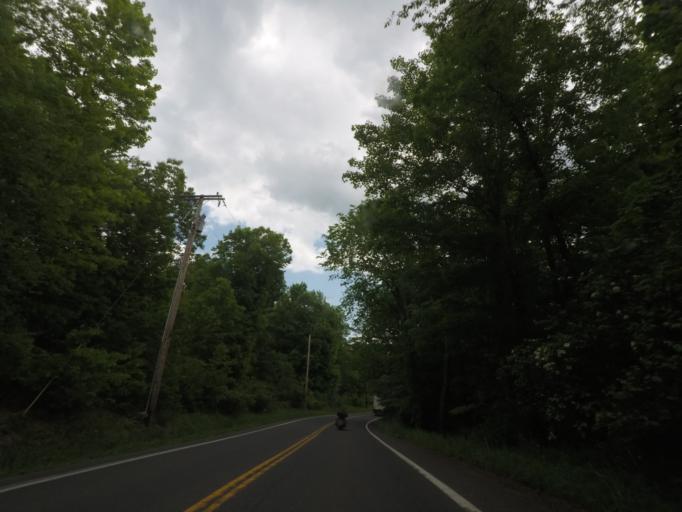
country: US
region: New York
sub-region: Dutchess County
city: Pine Plains
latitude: 42.0721
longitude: -73.6695
